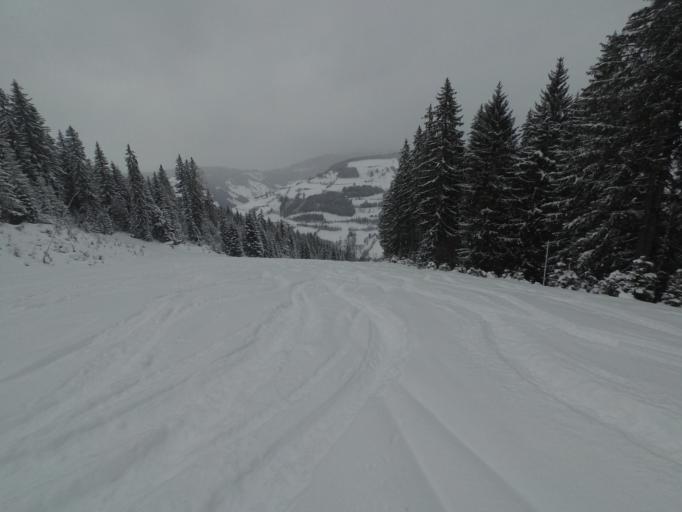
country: AT
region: Salzburg
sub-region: Politischer Bezirk Sankt Johann im Pongau
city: Wagrain
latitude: 47.3244
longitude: 13.2912
